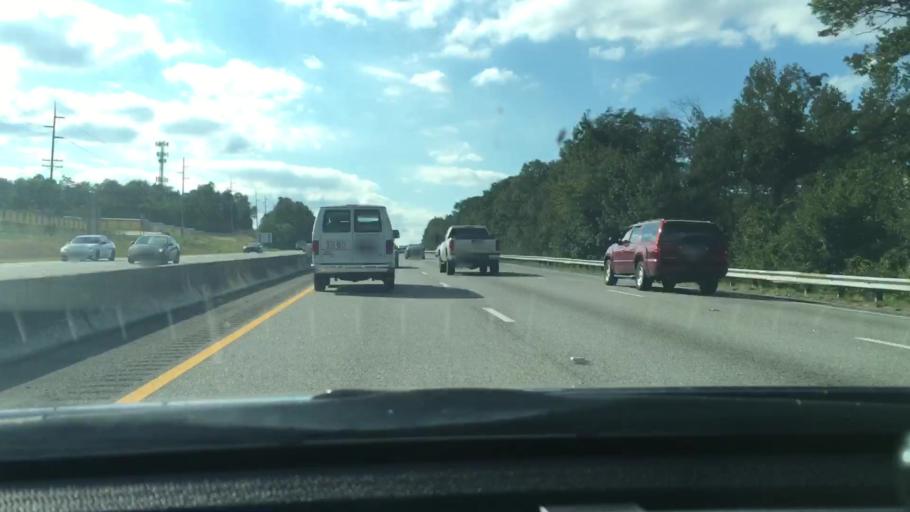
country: US
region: South Carolina
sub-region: Richland County
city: Dentsville
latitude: 34.0740
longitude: -80.9595
